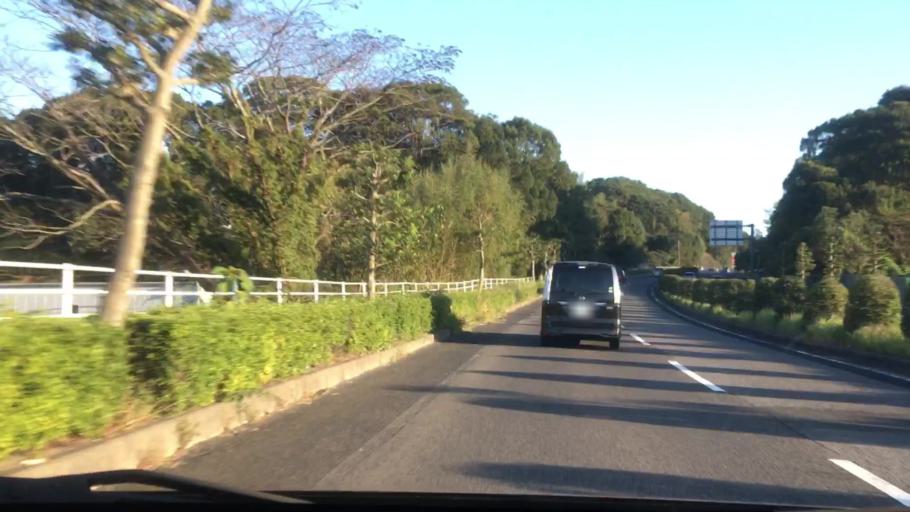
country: JP
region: Nagasaki
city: Sasebo
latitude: 33.1400
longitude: 129.7843
